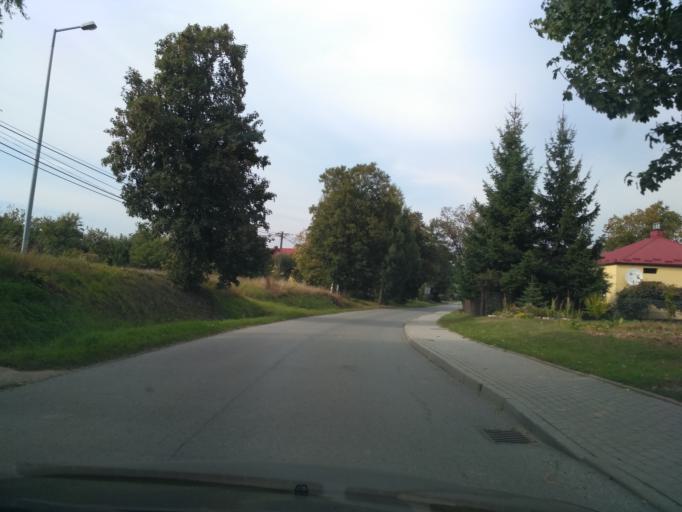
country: PL
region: Subcarpathian Voivodeship
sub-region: Powiat rzeszowski
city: Trzciana
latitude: 50.0644
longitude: 21.8352
